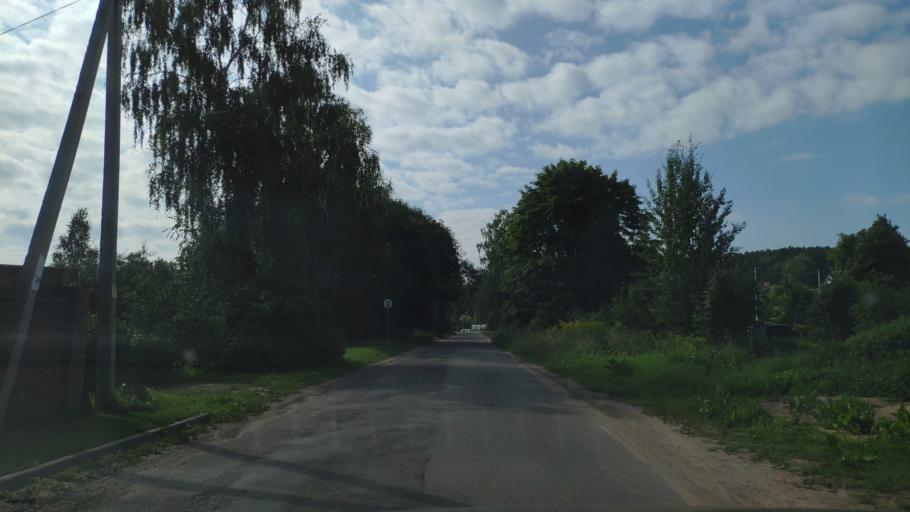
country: BY
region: Minsk
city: Zaslawye
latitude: 53.9926
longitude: 27.2843
